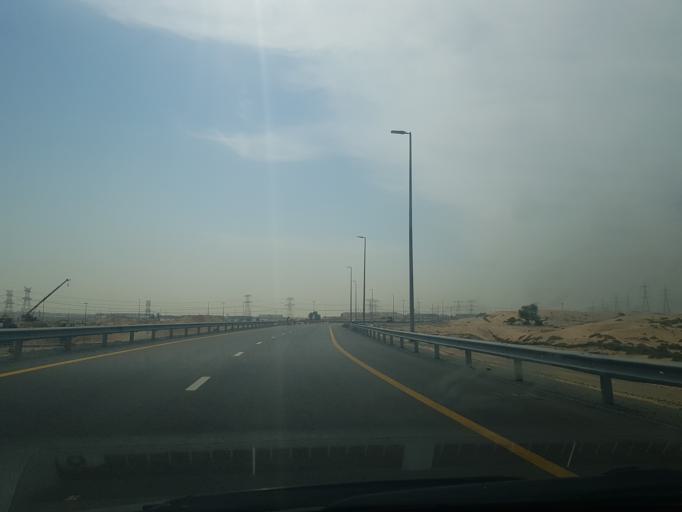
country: AE
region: Ash Shariqah
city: Sharjah
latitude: 25.2428
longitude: 55.5676
